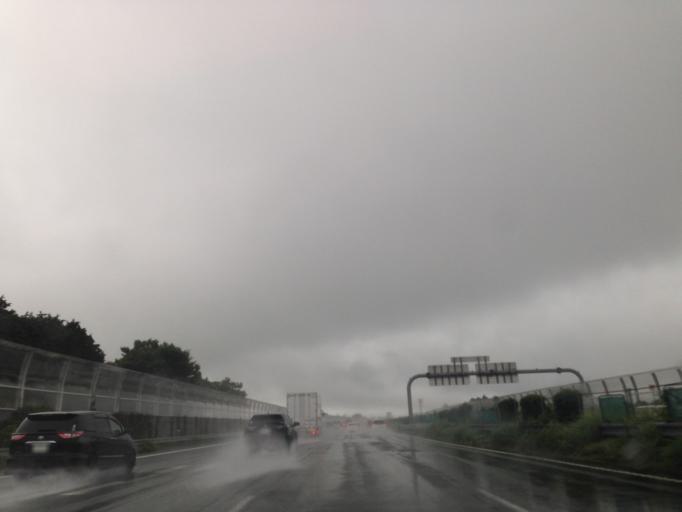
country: JP
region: Shizuoka
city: Gotemba
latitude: 35.2746
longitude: 138.9177
